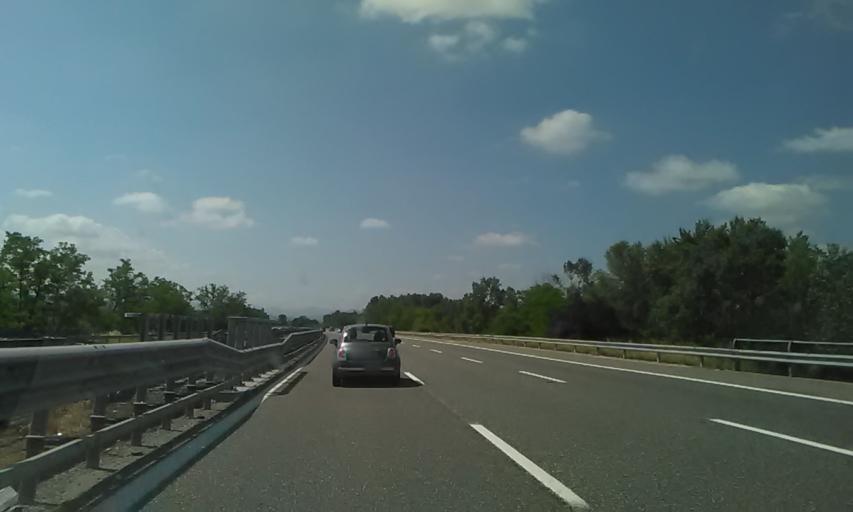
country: IT
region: Piedmont
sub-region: Provincia di Alessandria
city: Capriata d'Orba
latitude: 44.7173
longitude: 8.6668
